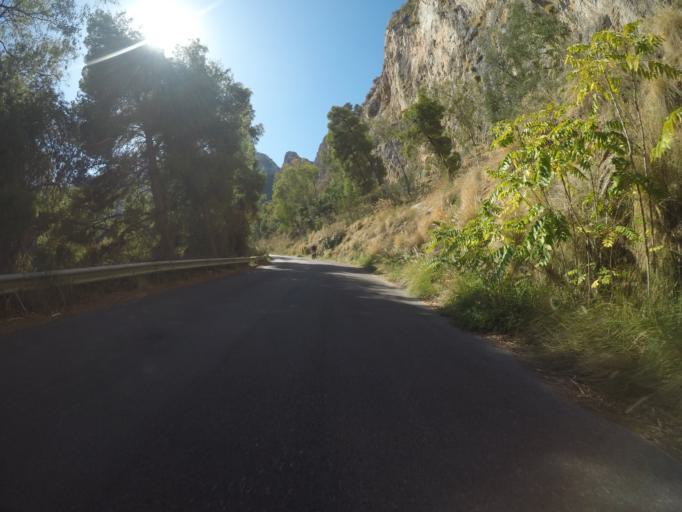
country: IT
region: Sicily
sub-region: Palermo
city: Palermo
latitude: 38.1919
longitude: 13.3391
